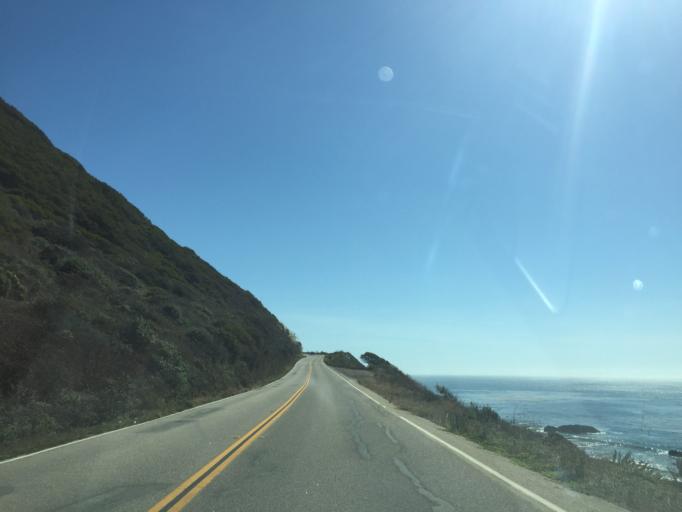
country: US
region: California
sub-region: Monterey County
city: Greenfield
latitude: 35.9641
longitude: -121.4841
